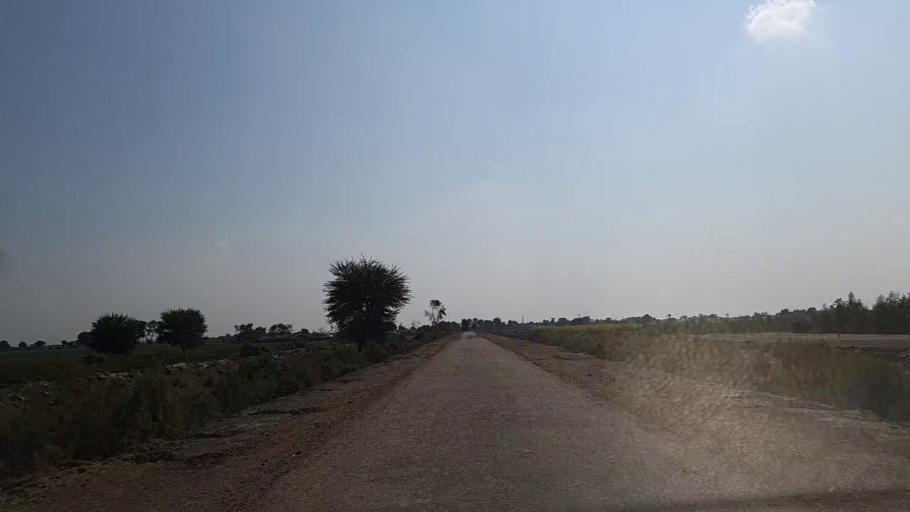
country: PK
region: Sindh
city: Jam Sahib
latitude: 26.2481
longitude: 68.5668
